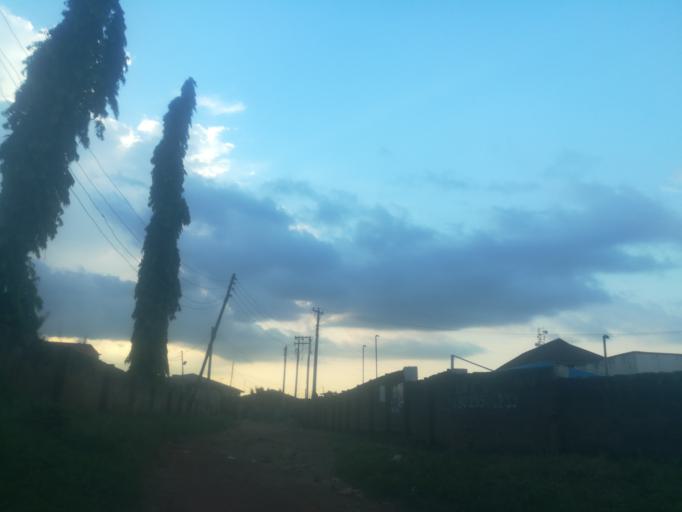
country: NG
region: Oyo
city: Ibadan
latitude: 7.4447
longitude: 3.9209
